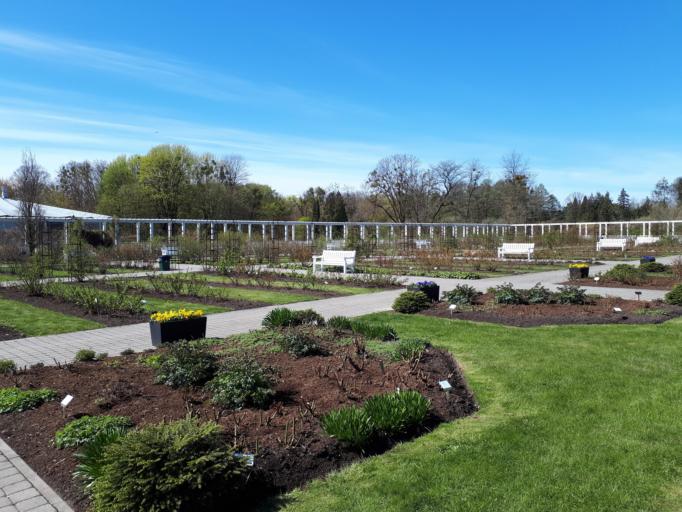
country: LT
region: Kauno apskritis
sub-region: Kaunas
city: Aleksotas
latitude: 54.8694
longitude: 23.9142
